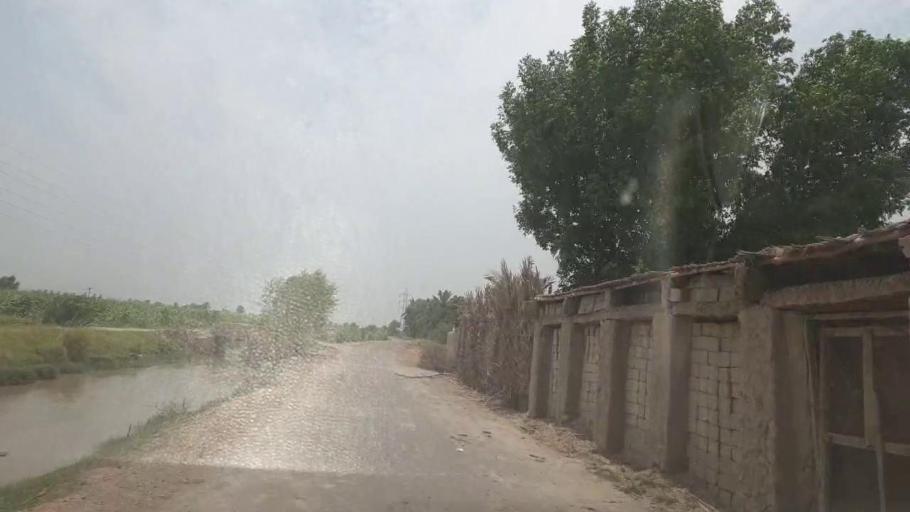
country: PK
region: Sindh
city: Kot Diji
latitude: 27.4227
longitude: 68.6476
